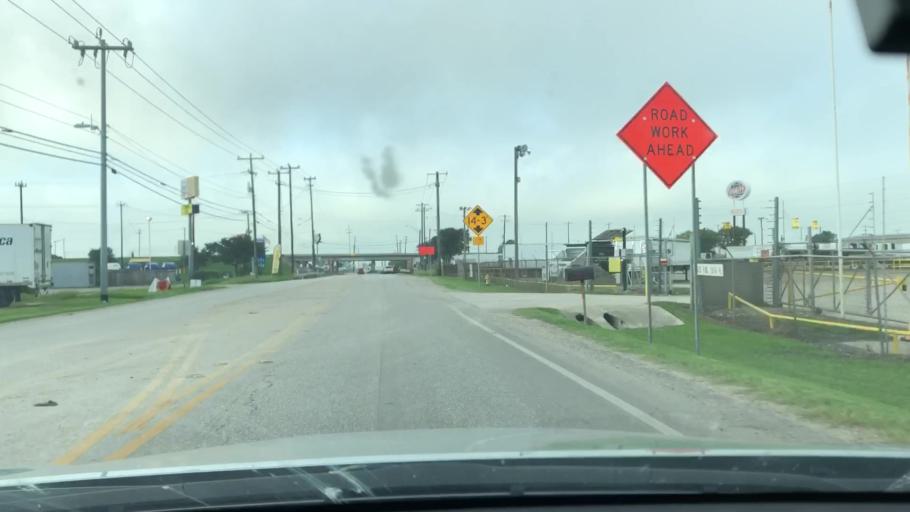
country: US
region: Texas
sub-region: Bexar County
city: Converse
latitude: 29.4613
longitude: -98.3164
